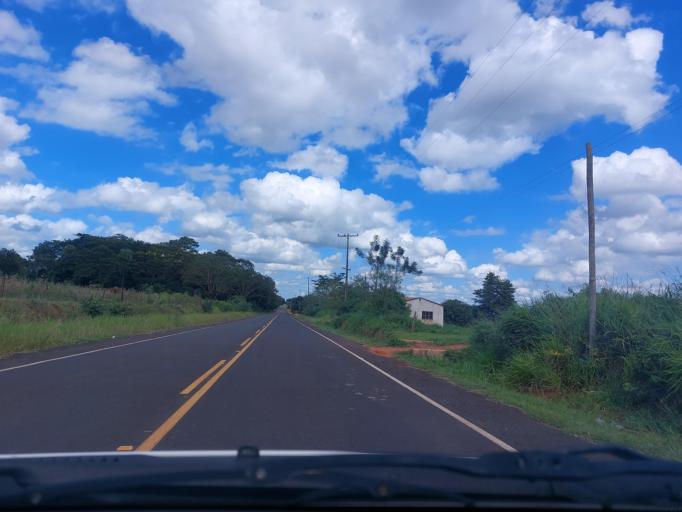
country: PY
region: San Pedro
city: Guayaybi
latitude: -24.5823
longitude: -56.5196
